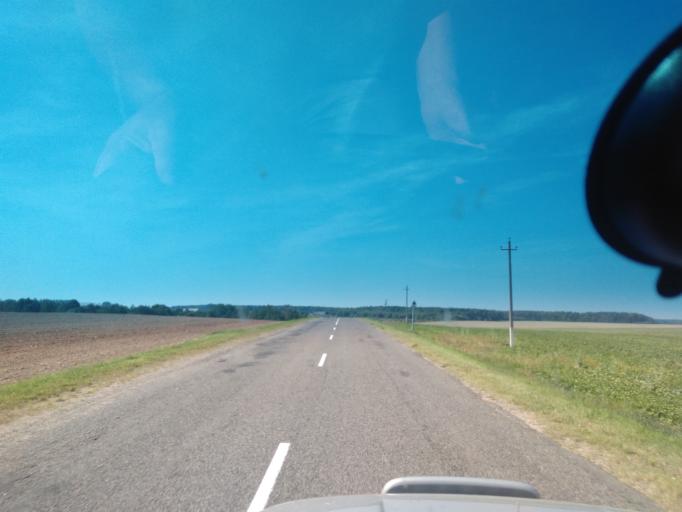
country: BY
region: Minsk
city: Kapyl'
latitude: 53.2171
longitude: 27.1391
